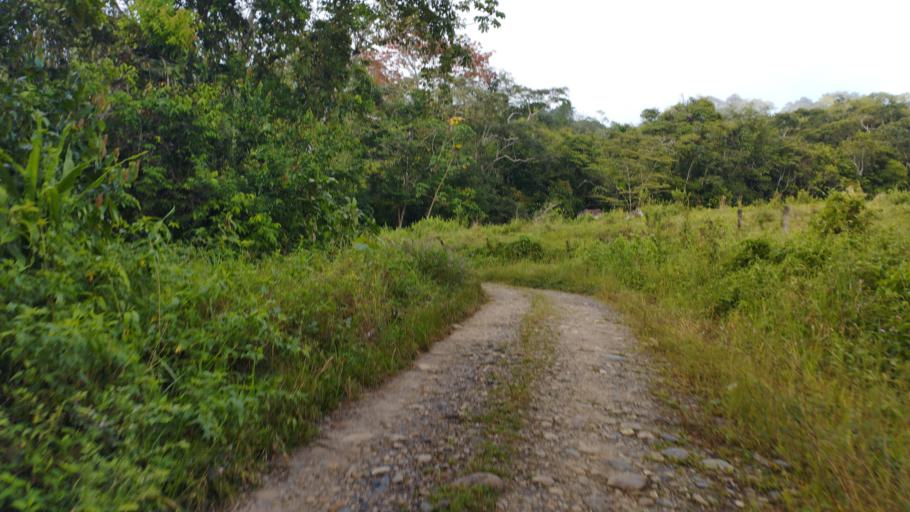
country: CO
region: Casanare
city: Sabanalarga
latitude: 4.7597
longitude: -73.0809
